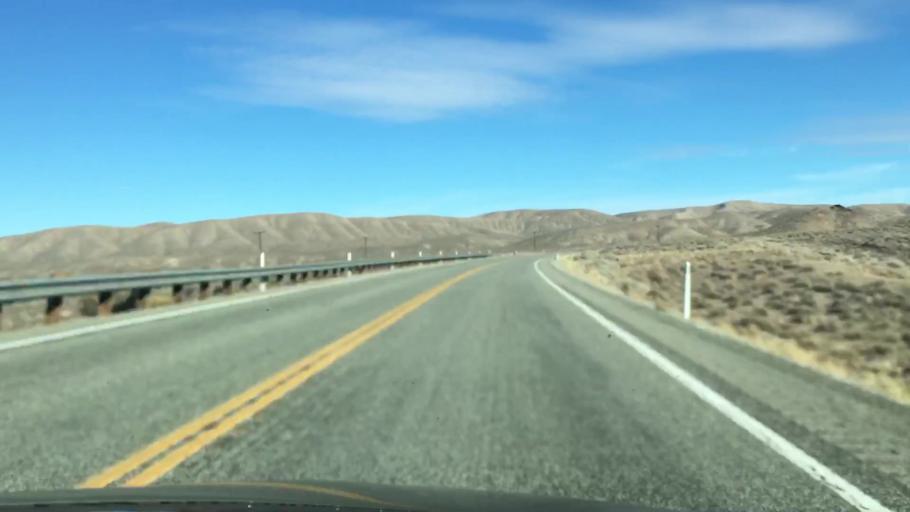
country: US
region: Nevada
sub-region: Lyon County
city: Yerington
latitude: 39.0451
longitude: -118.9779
